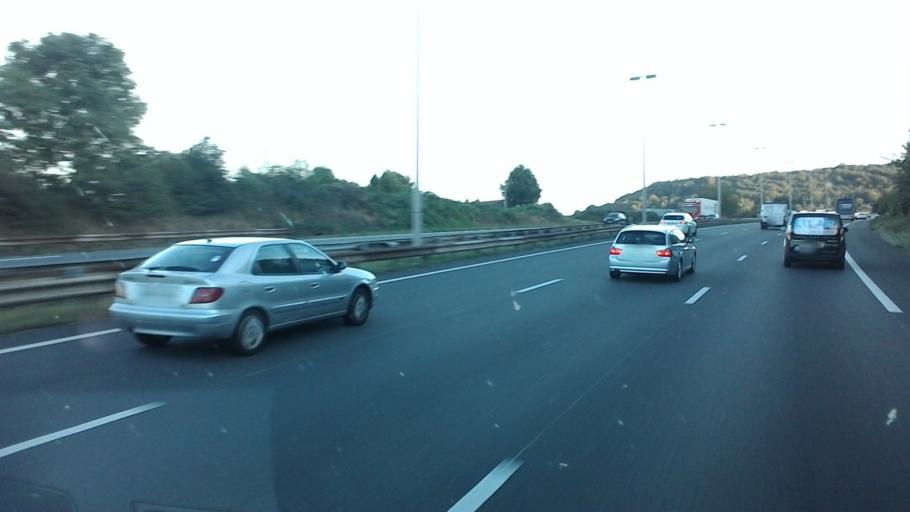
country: FR
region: Lorraine
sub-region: Departement de Meurthe-et-Moselle
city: Champigneulles
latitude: 48.7363
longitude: 6.1566
